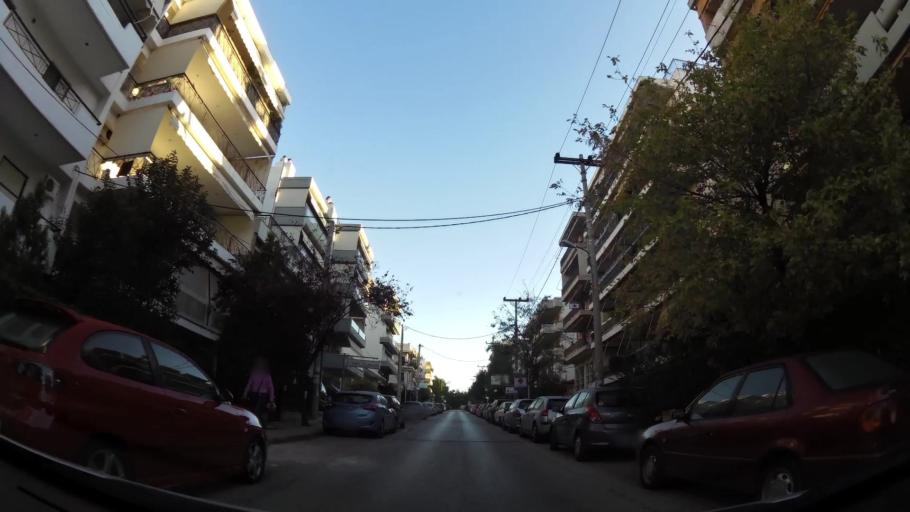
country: GR
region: Attica
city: Pefki
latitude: 38.0542
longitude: 23.7920
